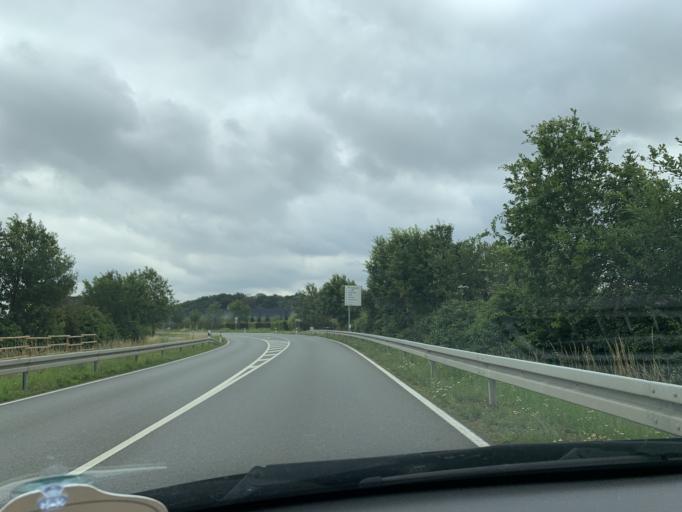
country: DE
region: North Rhine-Westphalia
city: Oelde
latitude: 51.8133
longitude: 8.1191
